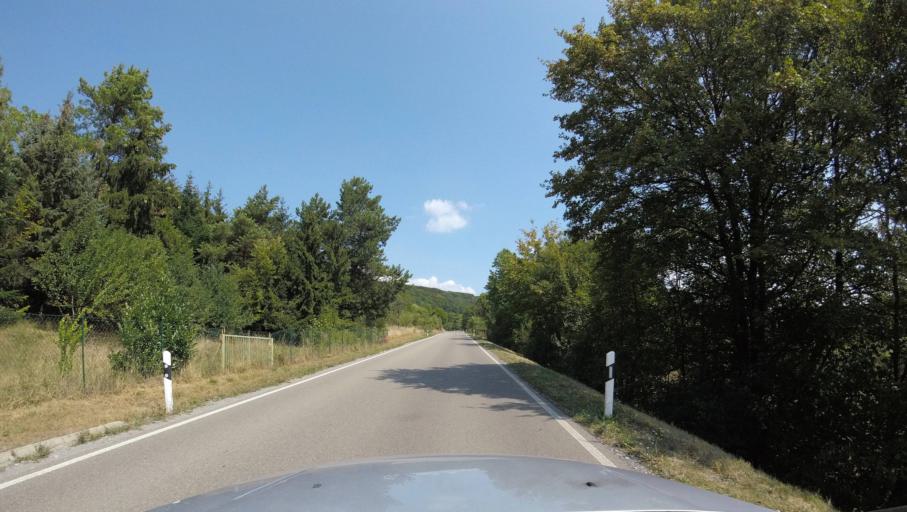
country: DE
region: Baden-Wuerttemberg
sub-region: Regierungsbezirk Stuttgart
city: Althutte
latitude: 48.9425
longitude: 9.5238
